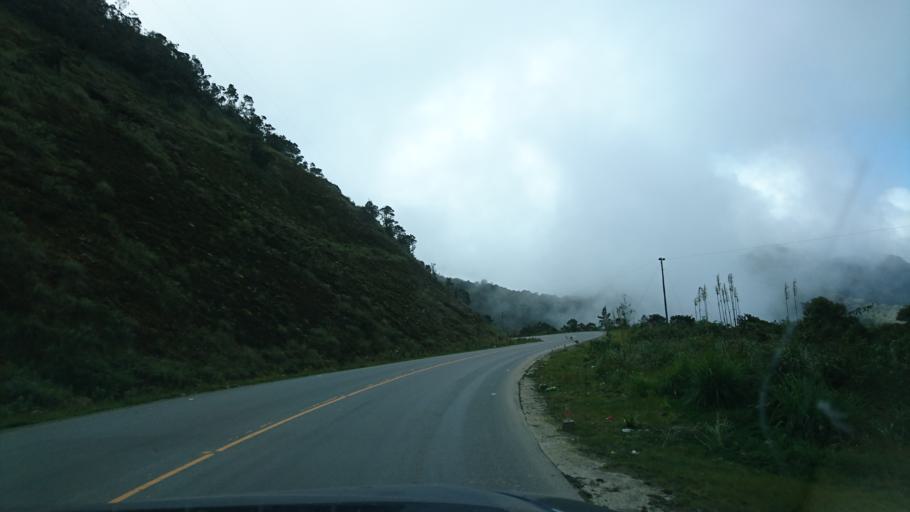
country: BO
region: La Paz
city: Coroico
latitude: -16.2882
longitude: -67.8545
